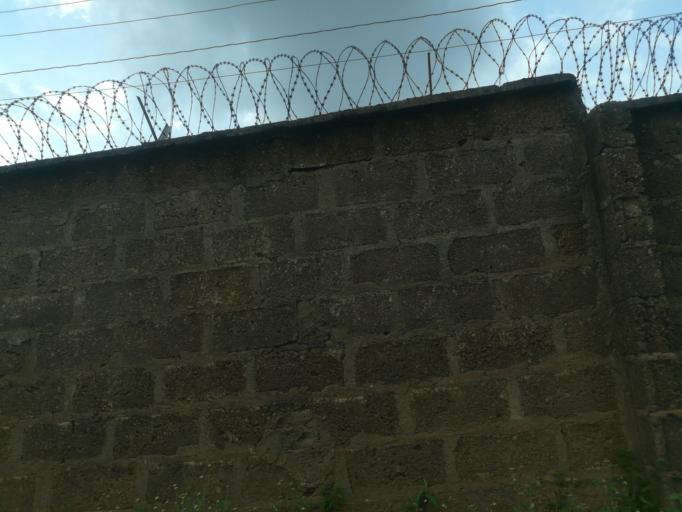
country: NG
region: Oyo
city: Ibadan
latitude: 7.4386
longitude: 3.9379
